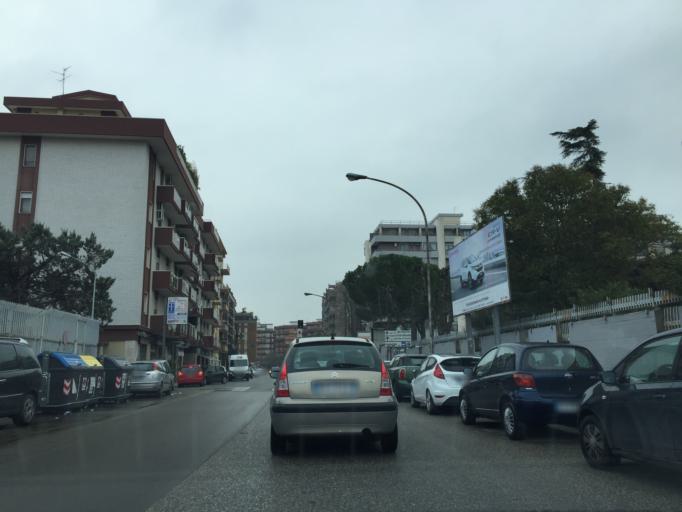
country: IT
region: Apulia
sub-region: Provincia di Foggia
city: Foggia
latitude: 41.4614
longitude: 15.5333
